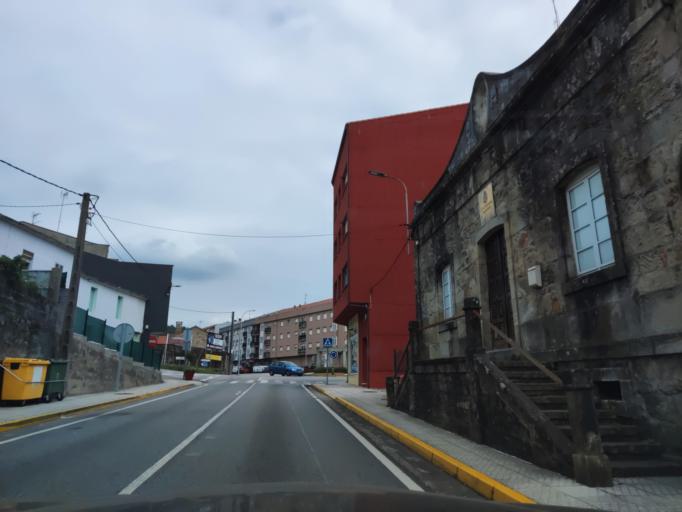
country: ES
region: Galicia
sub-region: Provincia da Coruna
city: Boiro
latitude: 42.6508
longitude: -8.8795
